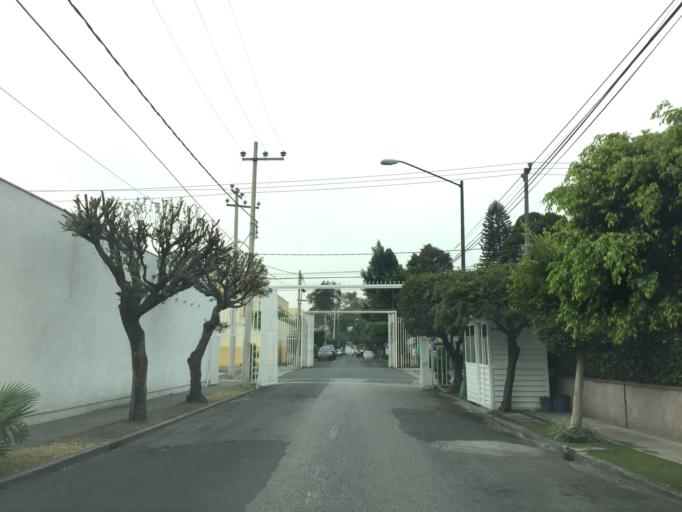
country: MX
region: Mexico
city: Colonia Lindavista
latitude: 19.4908
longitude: -99.1235
